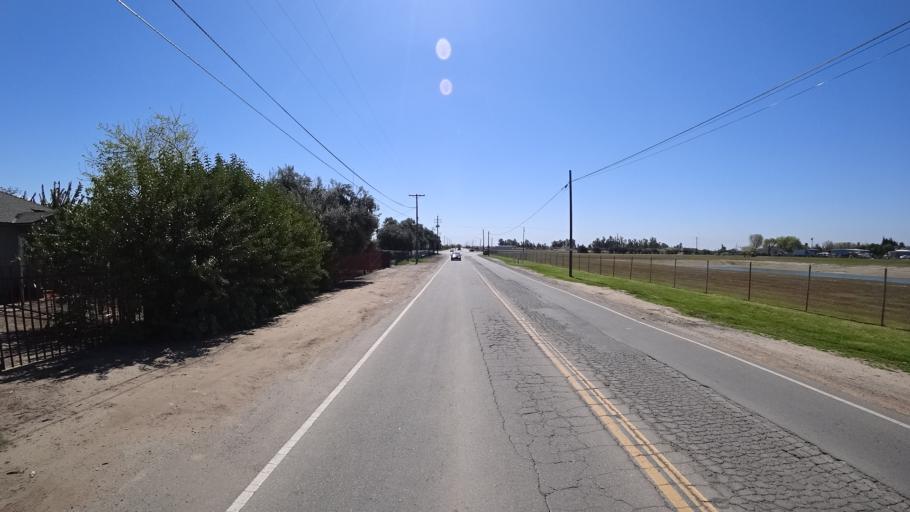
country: US
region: California
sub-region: Fresno County
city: West Park
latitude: 36.7522
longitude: -119.8443
